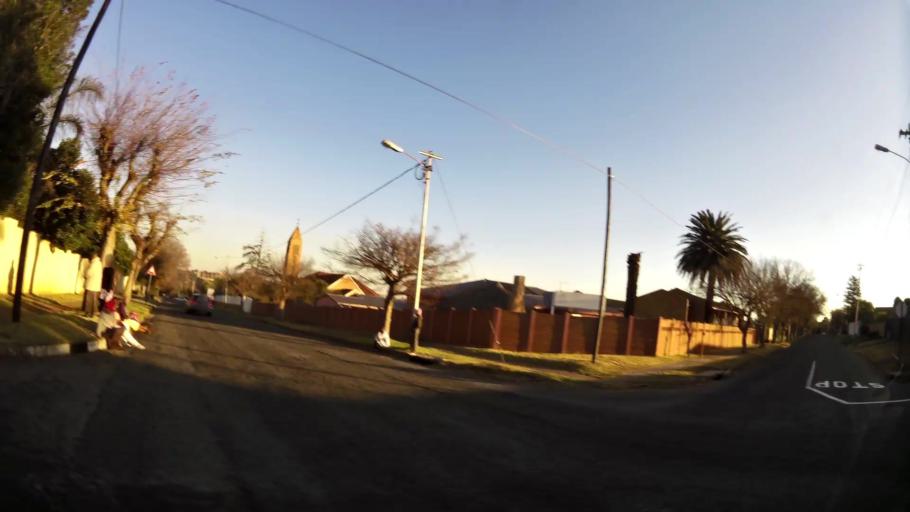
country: ZA
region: Gauteng
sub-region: City of Johannesburg Metropolitan Municipality
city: Roodepoort
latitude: -26.1752
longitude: 27.9302
